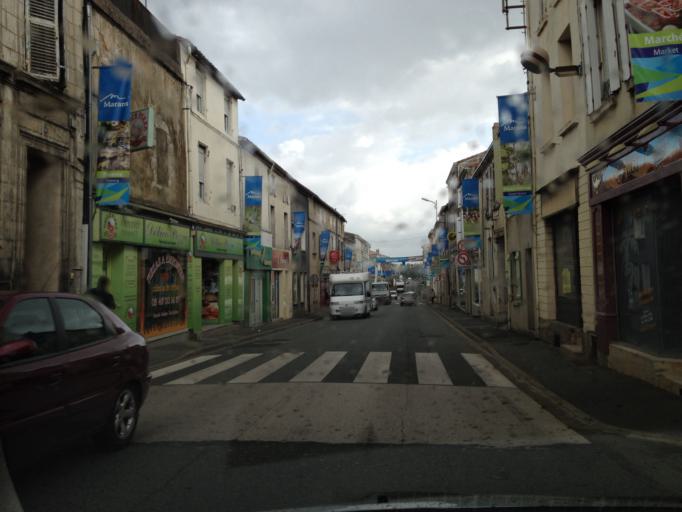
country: FR
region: Poitou-Charentes
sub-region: Departement de la Charente-Maritime
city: Marans
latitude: 46.3089
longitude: -0.9921
